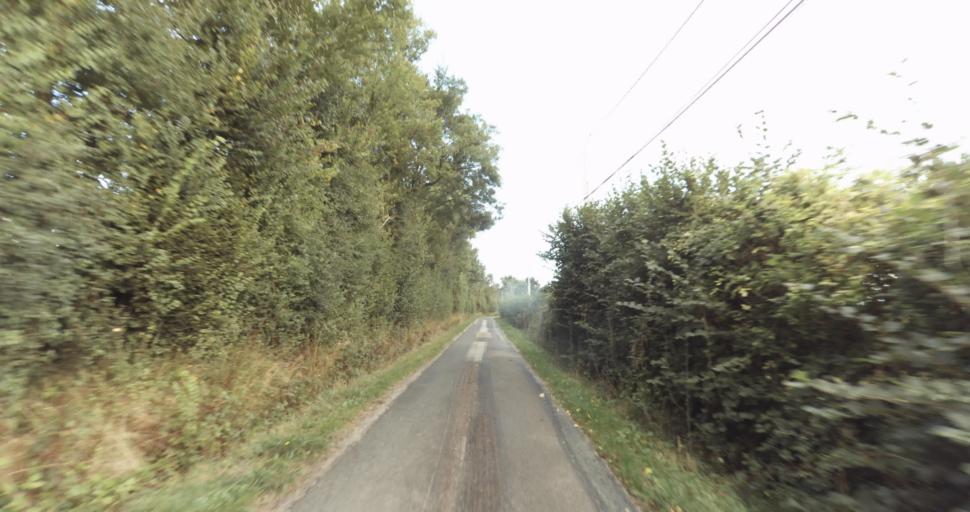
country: FR
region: Lower Normandy
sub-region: Departement de l'Orne
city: Gace
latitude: 48.7677
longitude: 0.3541
